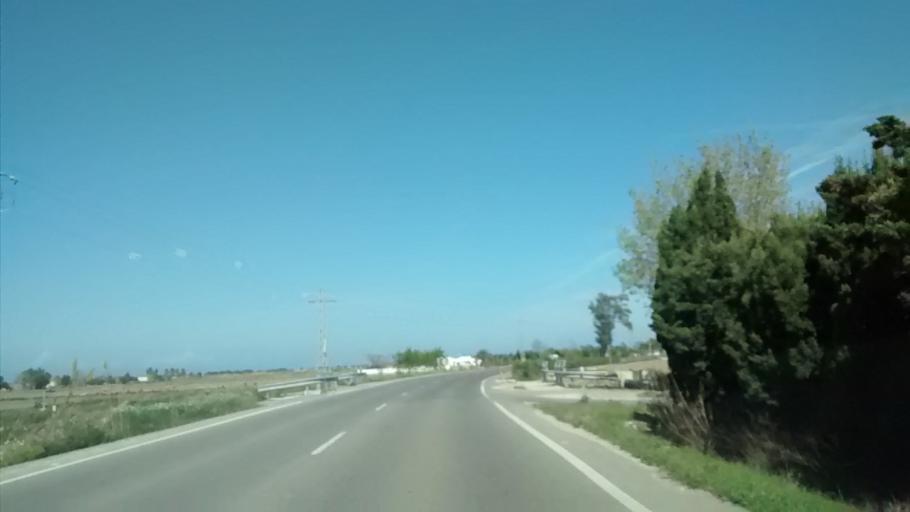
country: ES
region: Catalonia
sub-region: Provincia de Tarragona
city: Deltebre
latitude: 40.7114
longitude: 0.8182
